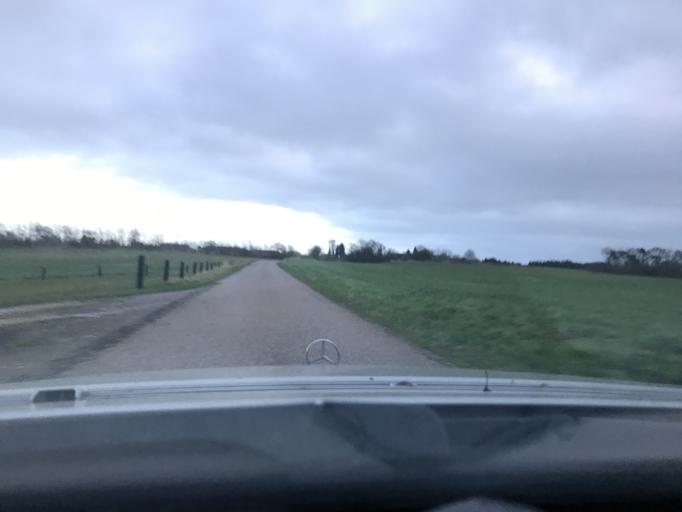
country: DK
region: South Denmark
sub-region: Sonderborg Kommune
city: Nordborg
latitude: 55.0593
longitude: 9.6980
